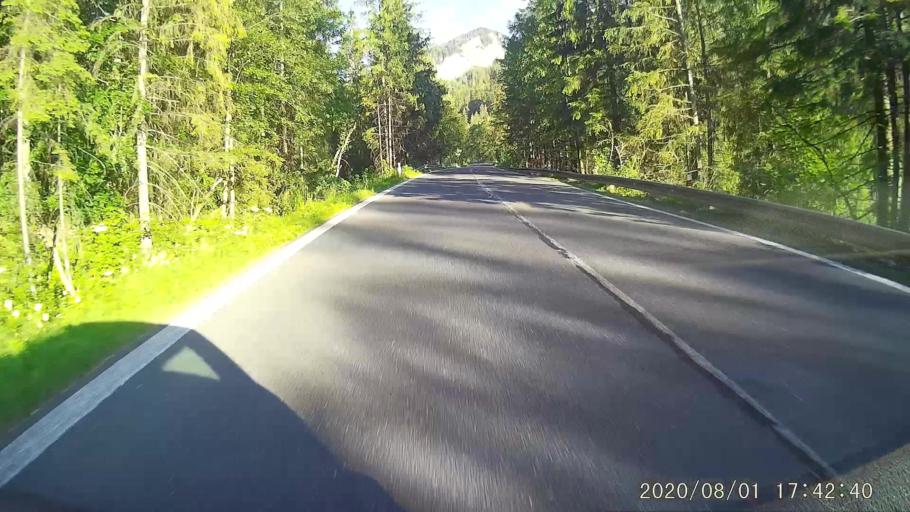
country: SK
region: Presovsky
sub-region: Okres Poprad
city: Zdiar
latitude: 49.2728
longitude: 20.1886
